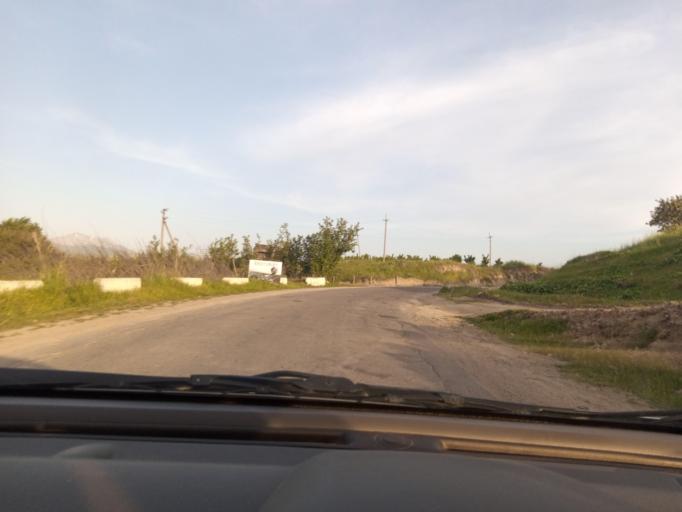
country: UZ
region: Toshkent
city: Parkent
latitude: 41.2361
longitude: 69.7369
